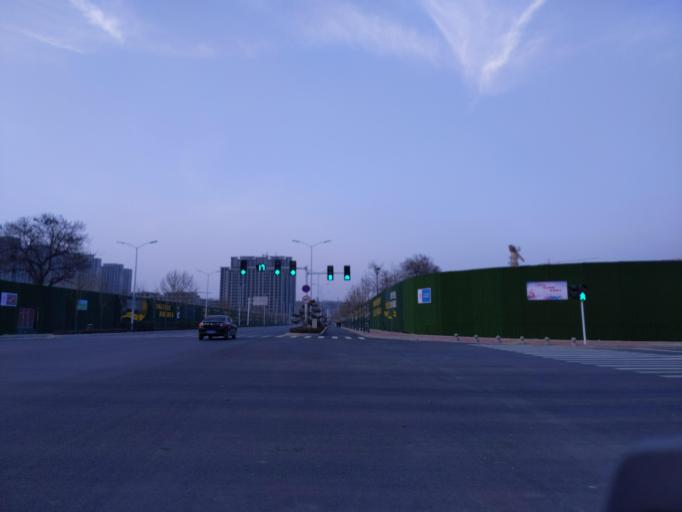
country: CN
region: Henan Sheng
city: Puyang
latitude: 35.8105
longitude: 115.0111
